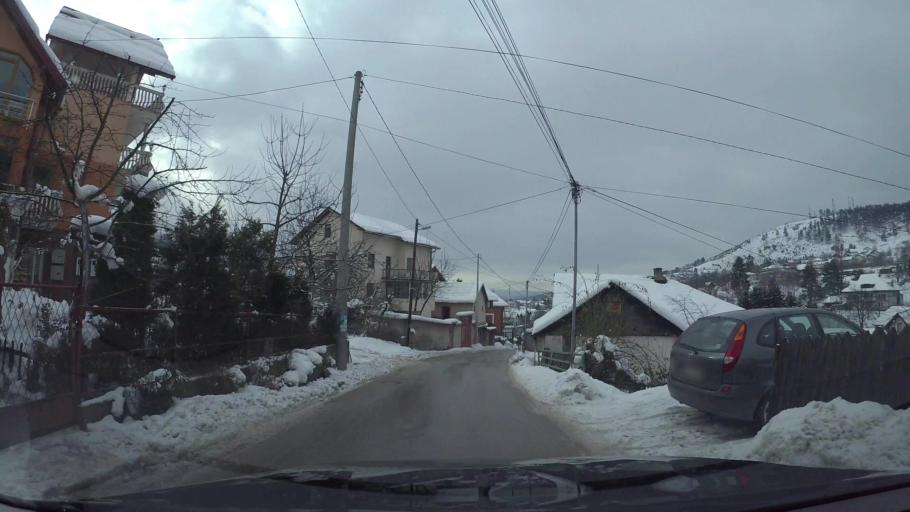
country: BA
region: Federation of Bosnia and Herzegovina
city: Kobilja Glava
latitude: 43.8735
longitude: 18.4407
